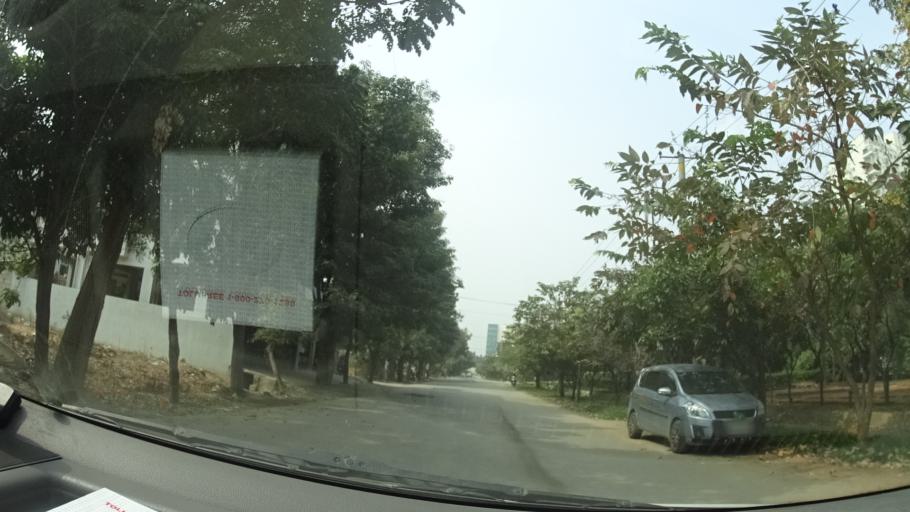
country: IN
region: Karnataka
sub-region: Bangalore Urban
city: Yelahanka
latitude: 13.0460
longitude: 77.6262
